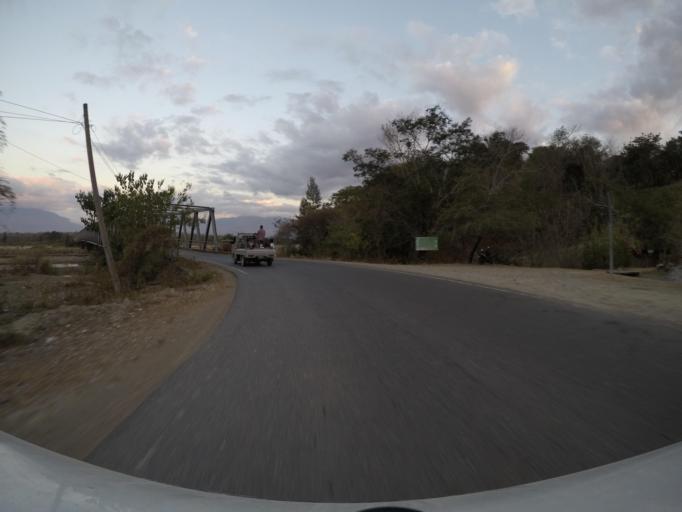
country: TL
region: Bobonaro
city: Maliana
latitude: -8.9603
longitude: 125.1091
